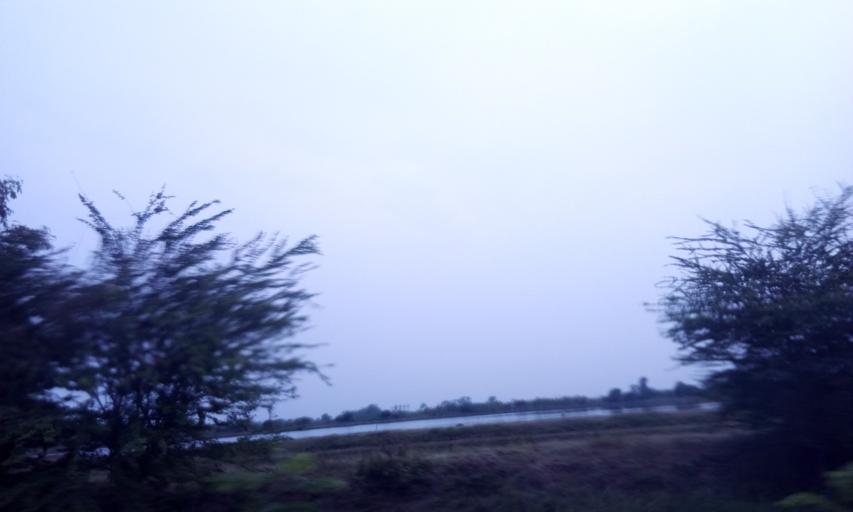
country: TH
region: Chachoengsao
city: Plaeng Yao
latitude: 13.5865
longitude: 101.2147
